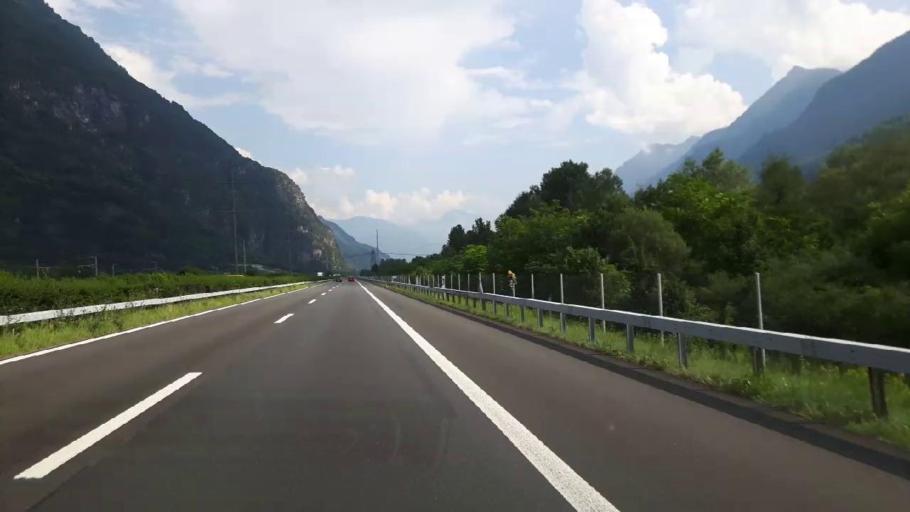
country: CH
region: Ticino
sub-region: Riviera District
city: Biasca
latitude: 46.3383
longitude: 8.9714
